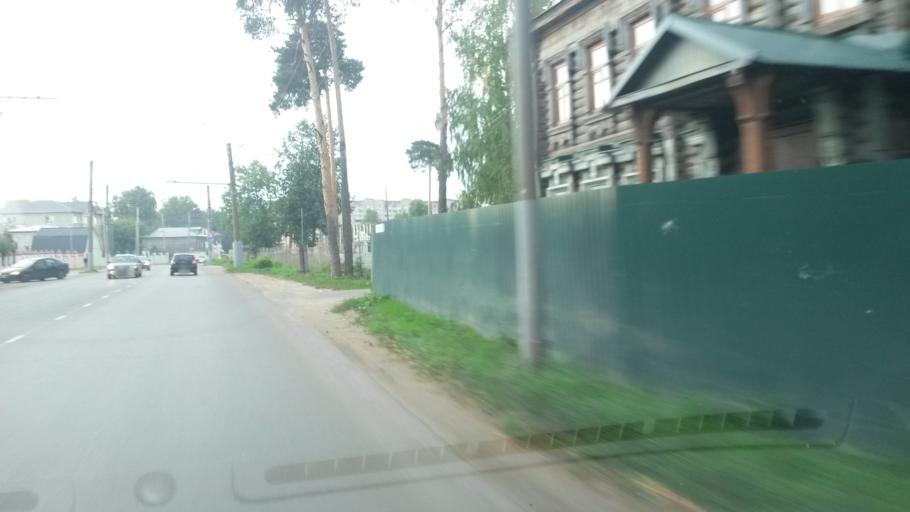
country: RU
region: Ivanovo
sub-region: Gorod Ivanovo
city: Ivanovo
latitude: 57.0222
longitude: 40.9478
